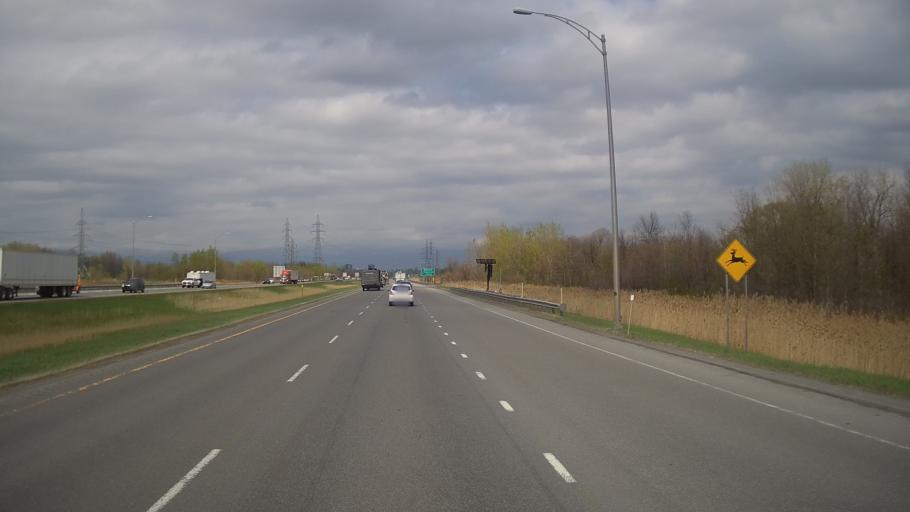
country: CA
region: Quebec
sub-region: Monteregie
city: La Prairie
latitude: 45.4071
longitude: -73.4587
